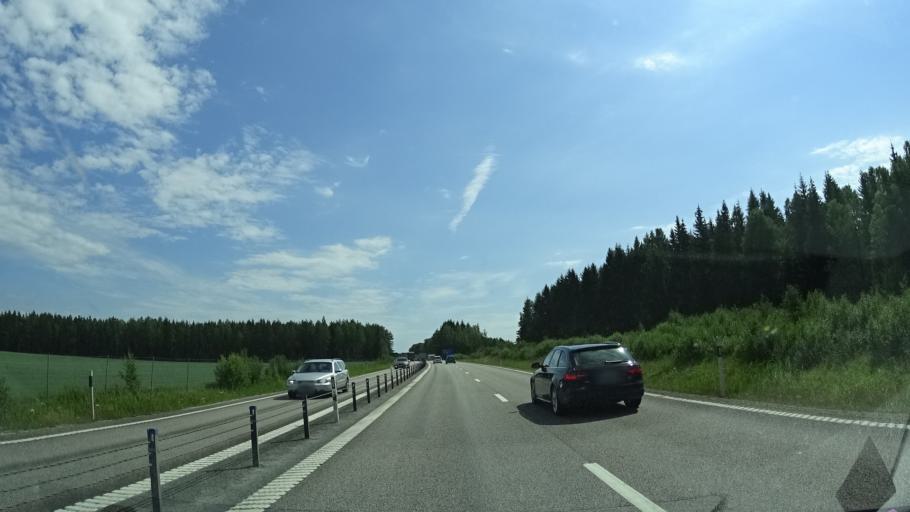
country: SE
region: Vaermland
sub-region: Kristinehamns Kommun
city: Kristinehamn
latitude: 59.3810
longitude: 13.8895
